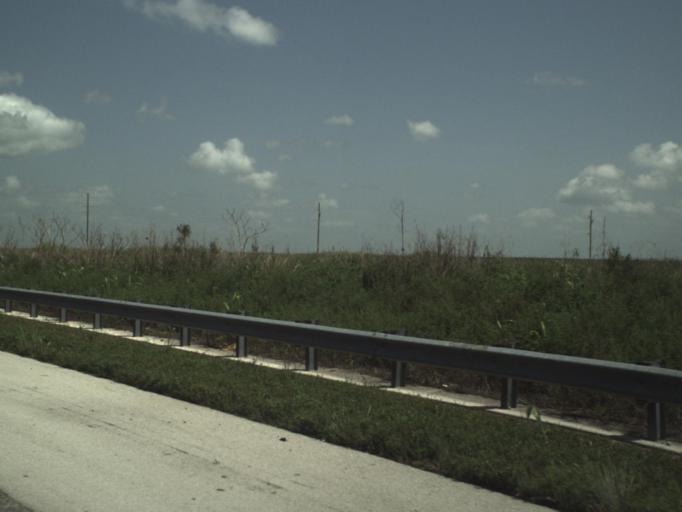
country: US
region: Florida
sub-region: Palm Beach County
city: Belle Glade Camp
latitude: 26.3756
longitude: -80.5691
